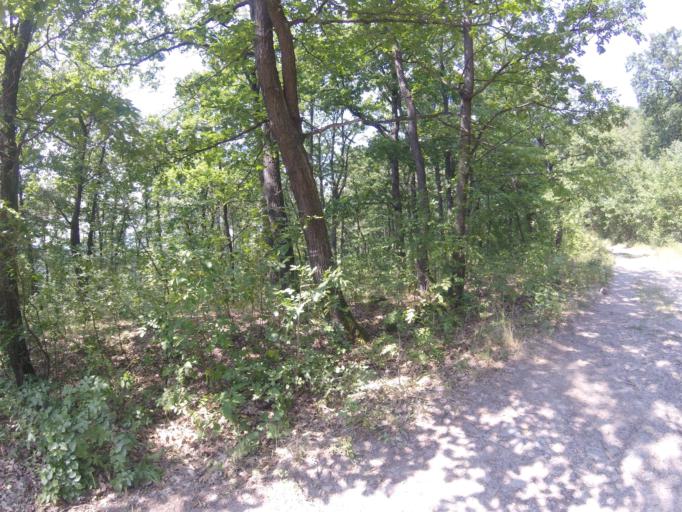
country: HU
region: Pest
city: Csobanka
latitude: 47.6758
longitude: 18.9626
